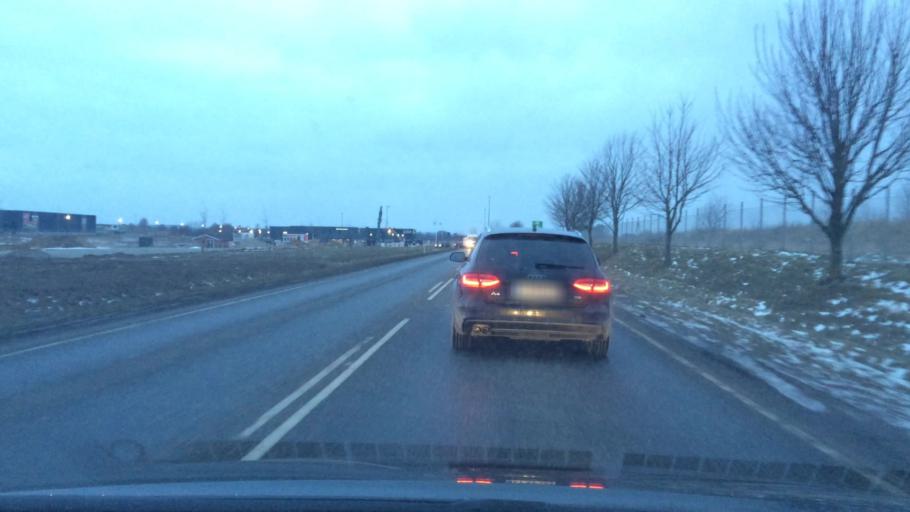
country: DK
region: Central Jutland
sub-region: Horsens Kommune
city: Horsens
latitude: 55.8358
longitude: 9.7921
